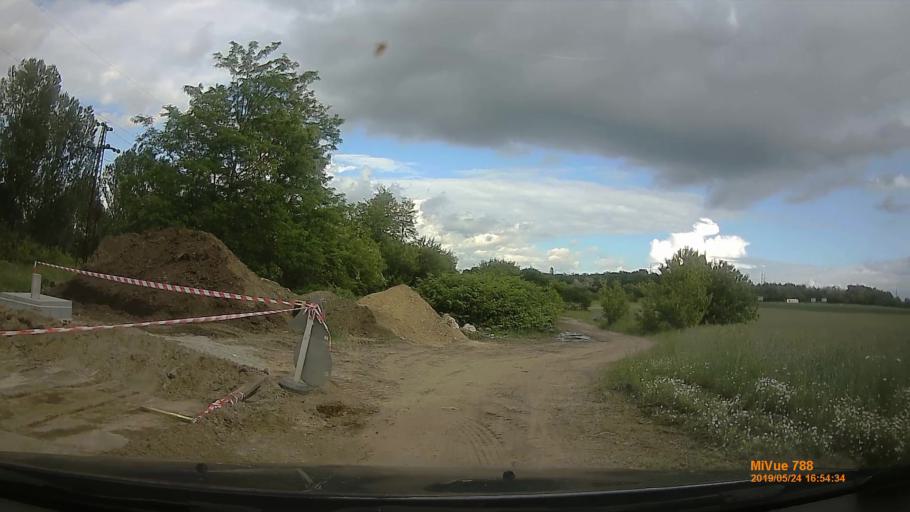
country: HU
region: Pest
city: Csomor
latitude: 47.5117
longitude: 19.2313
